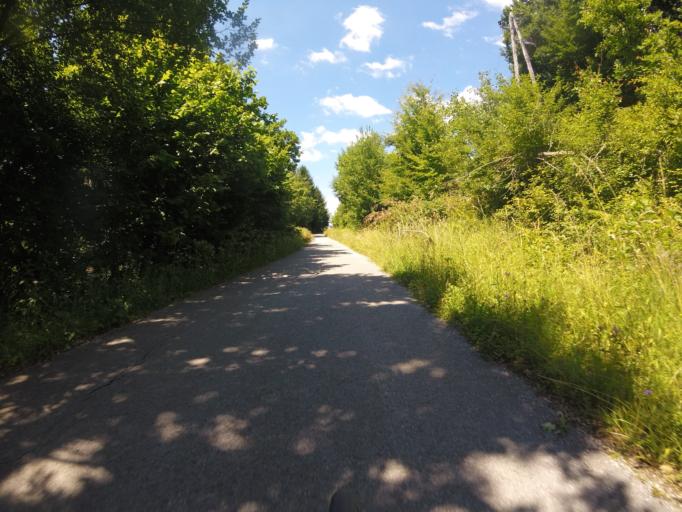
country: SI
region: Kostanjevica na Krki
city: Kostanjevica na Krki
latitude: 45.7611
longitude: 15.4447
